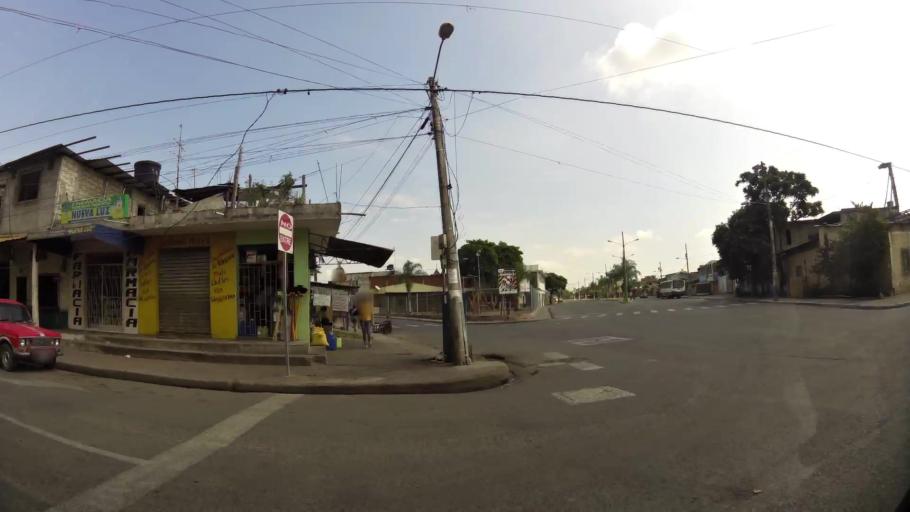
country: EC
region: Guayas
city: Eloy Alfaro
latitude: -2.1559
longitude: -79.8371
